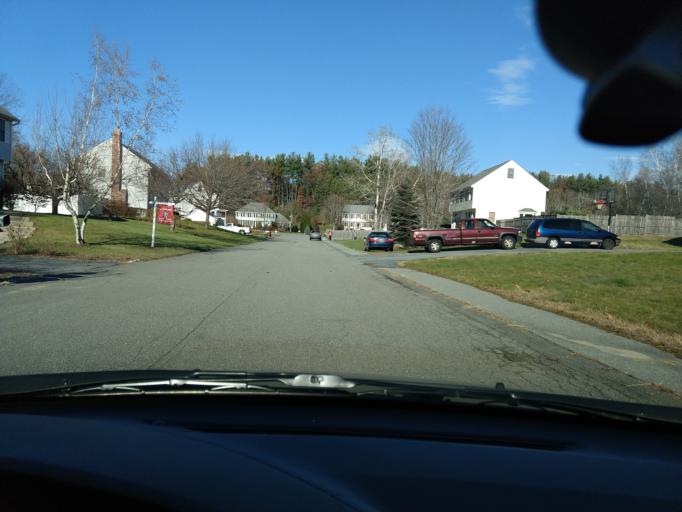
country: US
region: Massachusetts
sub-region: Middlesex County
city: East Pepperell
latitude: 42.6838
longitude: -71.5603
